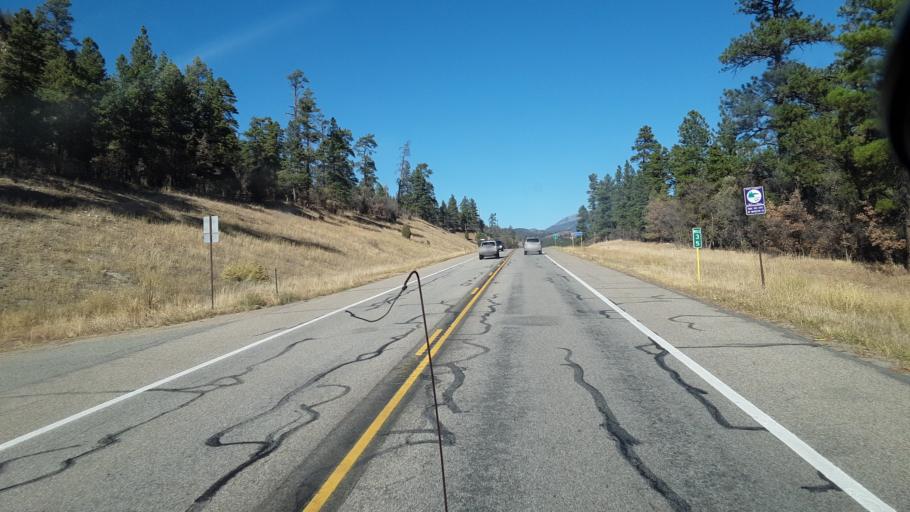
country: US
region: Colorado
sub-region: La Plata County
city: Durango
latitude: 37.4464
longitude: -107.8069
